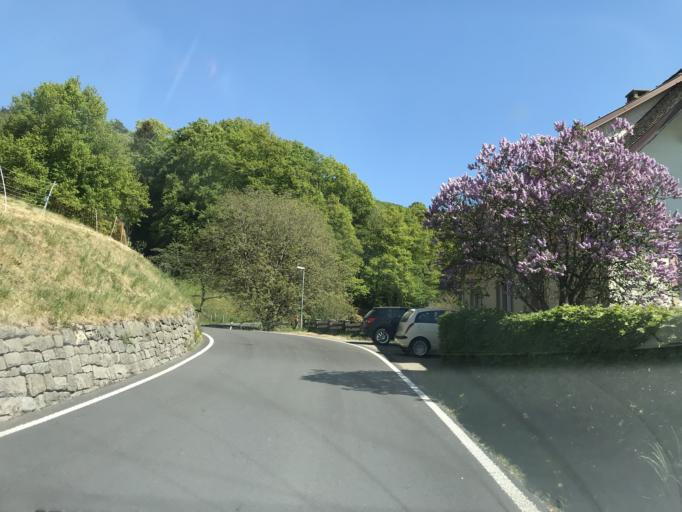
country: DE
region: Baden-Wuerttemberg
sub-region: Freiburg Region
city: Hausen
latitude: 47.6818
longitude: 7.8649
